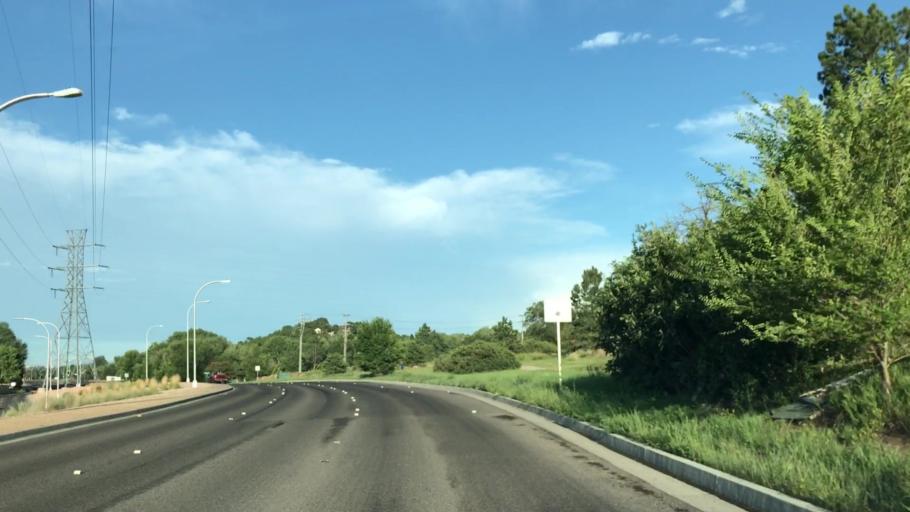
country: US
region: Colorado
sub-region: El Paso County
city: Colorado Springs
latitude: 38.8890
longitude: -104.7763
